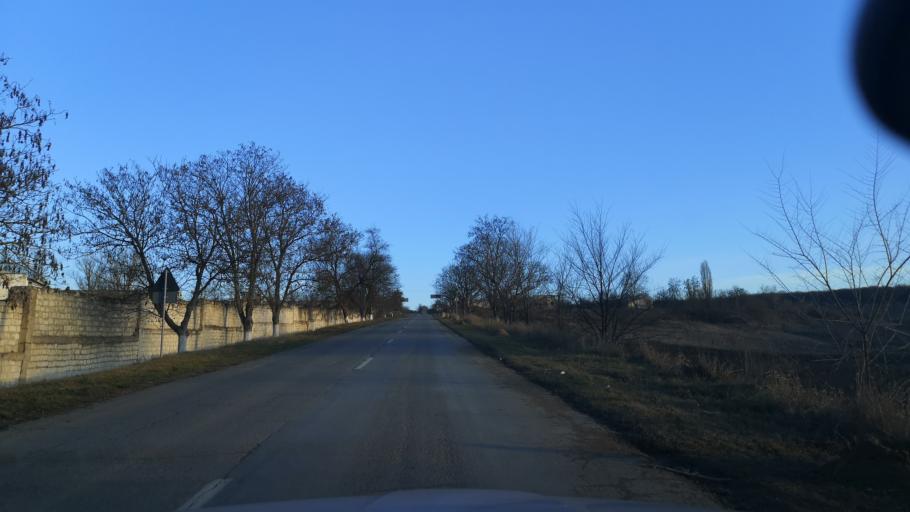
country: MD
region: Orhei
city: Orhei
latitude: 47.3089
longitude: 28.9341
